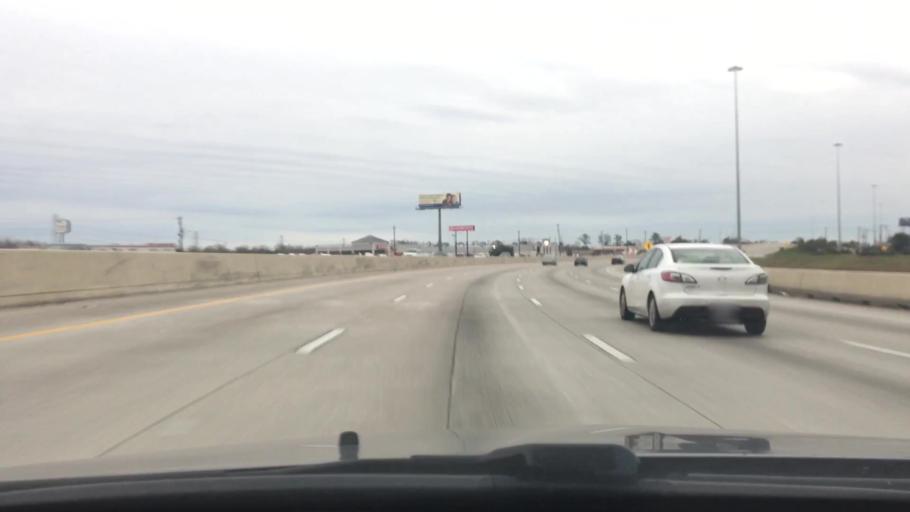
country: US
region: Texas
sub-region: Harris County
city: Houston
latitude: 29.8094
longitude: -95.3068
